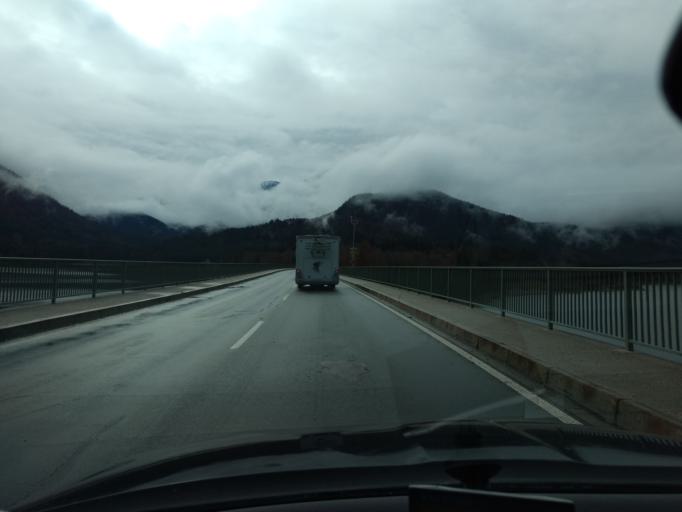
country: DE
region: Bavaria
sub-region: Upper Bavaria
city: Jachenau
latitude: 47.5769
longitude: 11.5373
